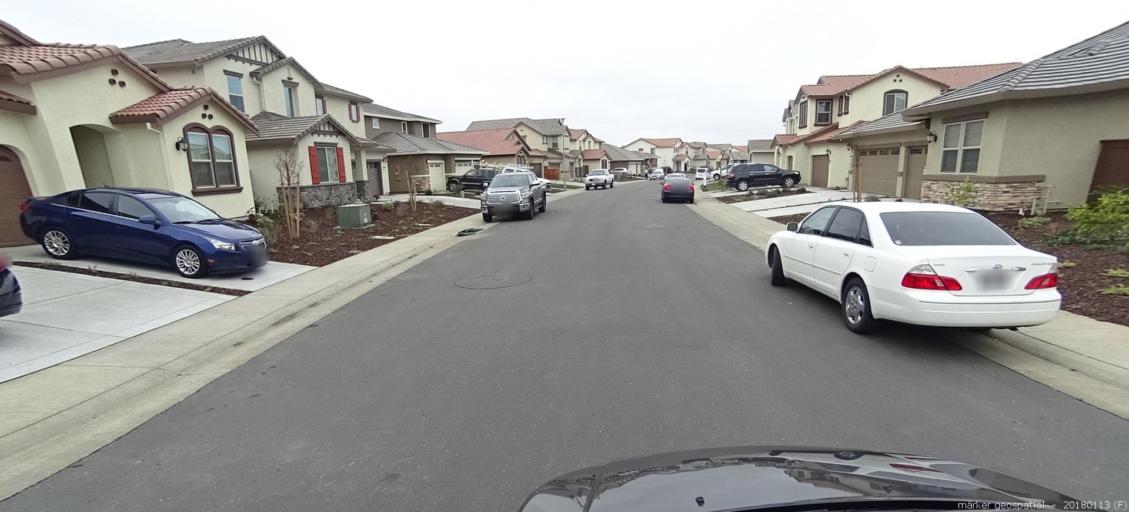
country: US
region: California
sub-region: Sacramento County
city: Gold River
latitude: 38.5676
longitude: -121.1990
